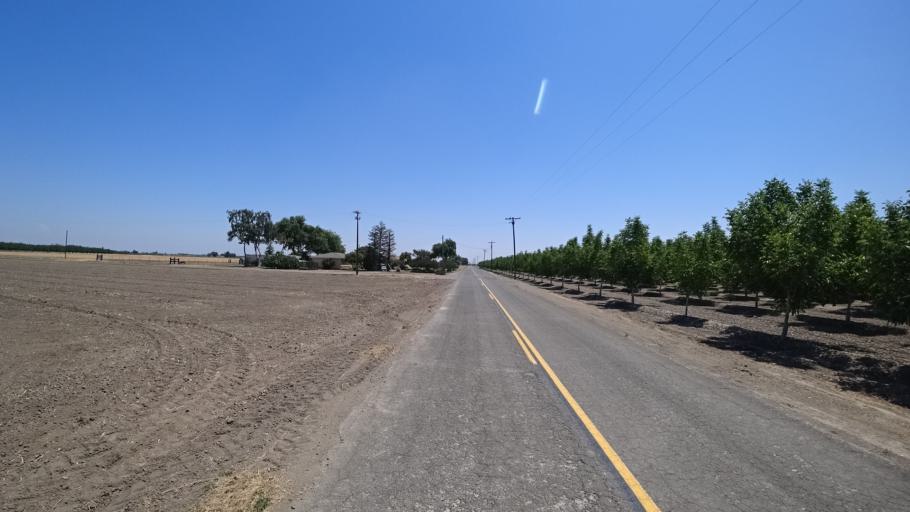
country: US
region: California
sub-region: Fresno County
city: Laton
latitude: 36.3865
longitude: -119.7373
